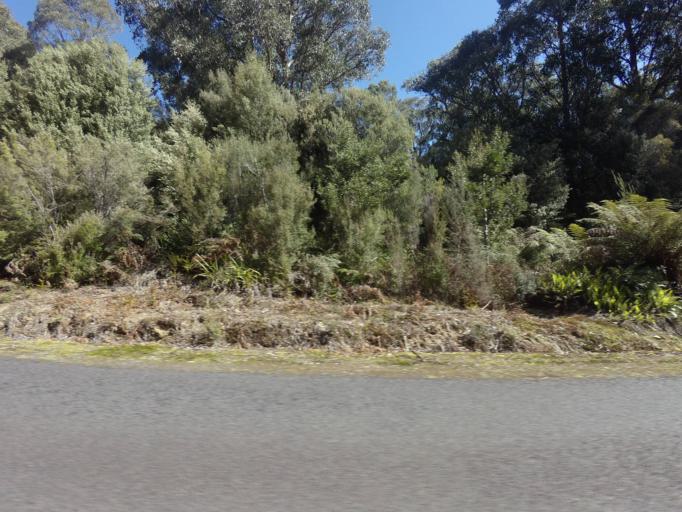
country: AU
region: Tasmania
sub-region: Derwent Valley
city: New Norfolk
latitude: -42.7642
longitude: 146.5496
